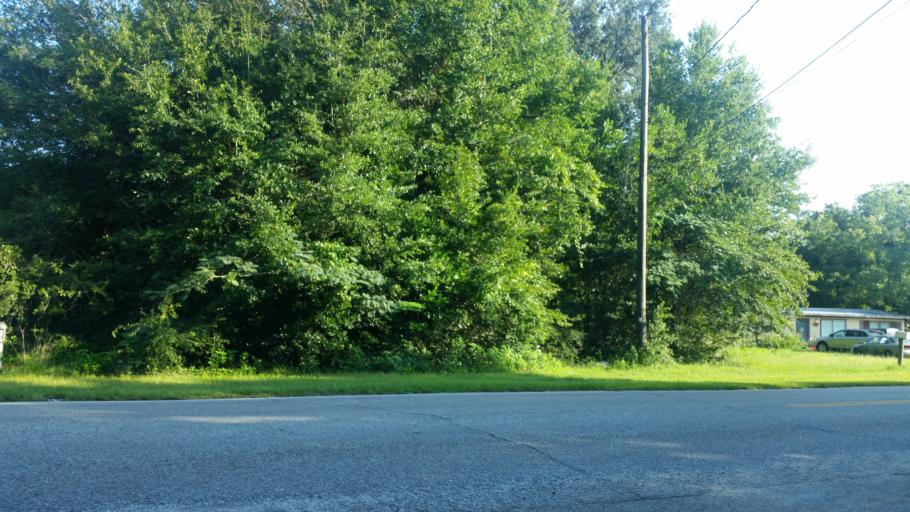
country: US
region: Florida
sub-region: Escambia County
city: Bellview
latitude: 30.4423
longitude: -87.3177
